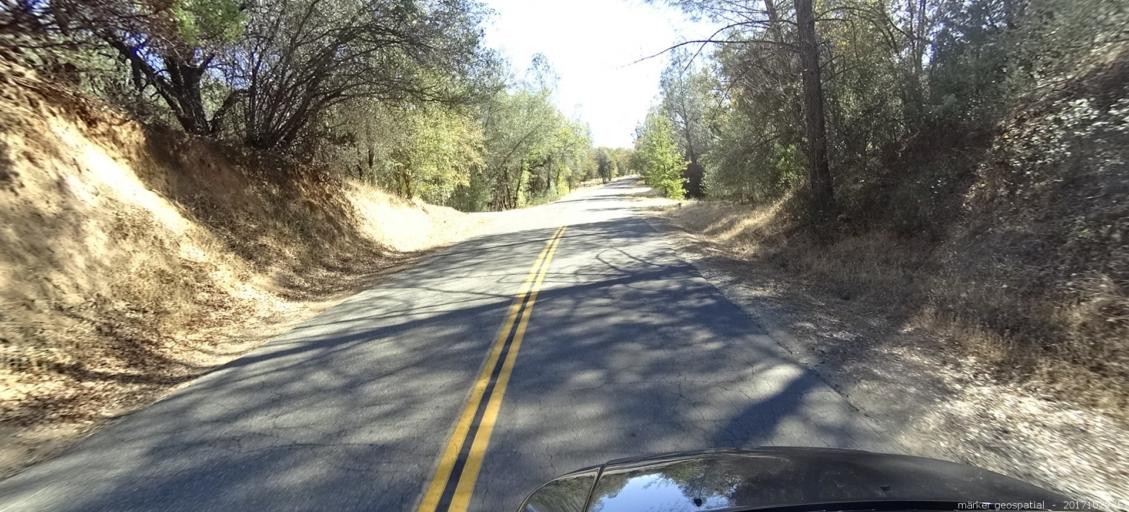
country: US
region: California
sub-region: Shasta County
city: Shasta
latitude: 40.4817
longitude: -122.6543
